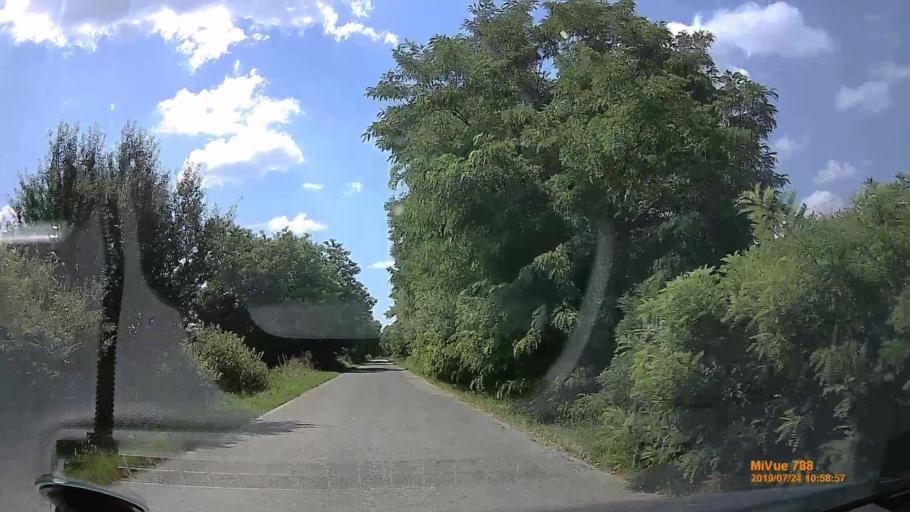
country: HU
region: Szabolcs-Szatmar-Bereg
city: Tarpa
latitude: 48.1716
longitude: 22.5164
